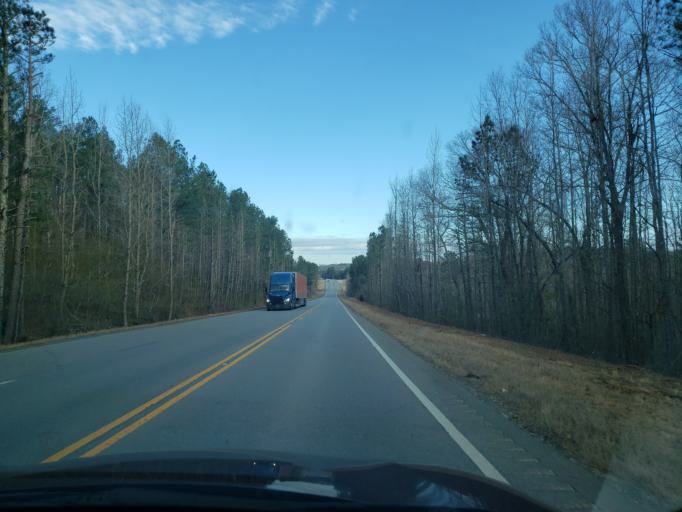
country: US
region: Alabama
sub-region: Randolph County
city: Wedowee
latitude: 33.4652
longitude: -85.5758
